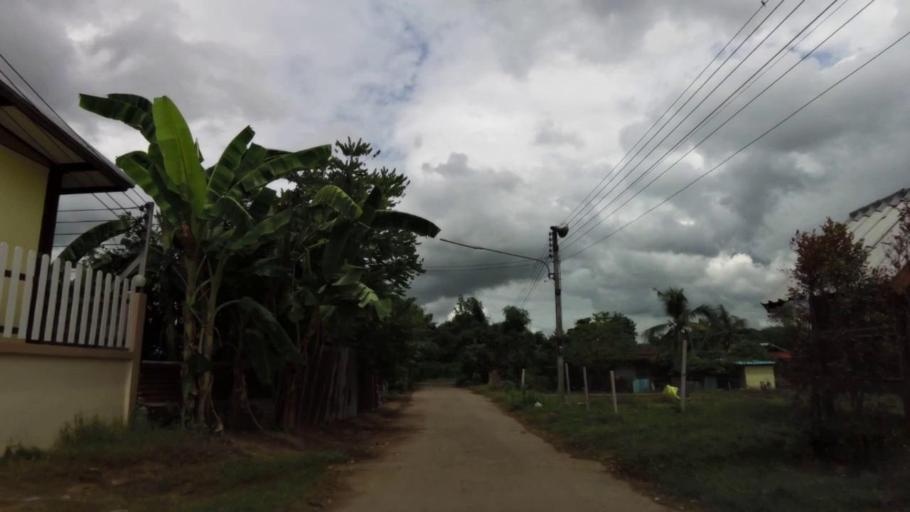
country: TH
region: Nakhon Sawan
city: Phai Sali
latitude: 15.6023
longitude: 100.6552
